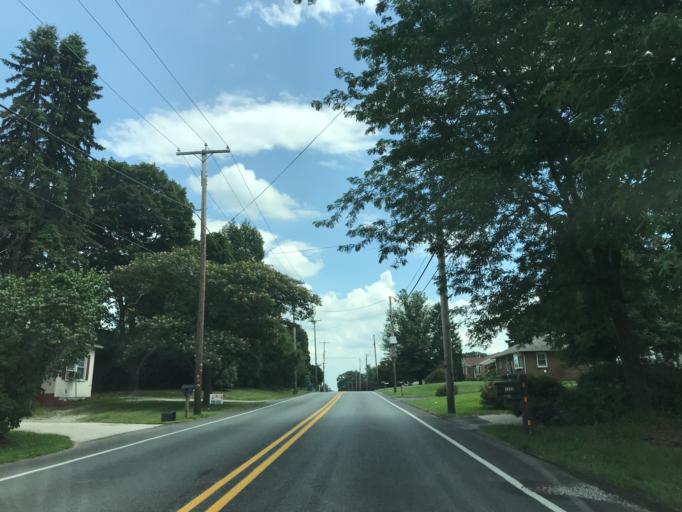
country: US
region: Pennsylvania
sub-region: York County
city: Windsor
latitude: 39.8889
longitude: -76.5522
